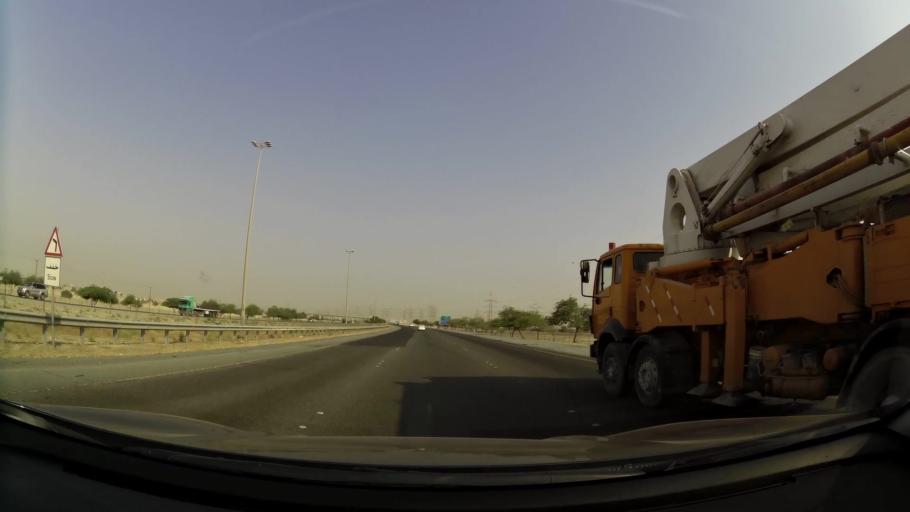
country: KW
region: Al Asimah
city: Ar Rabiyah
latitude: 29.2267
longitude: 47.8853
